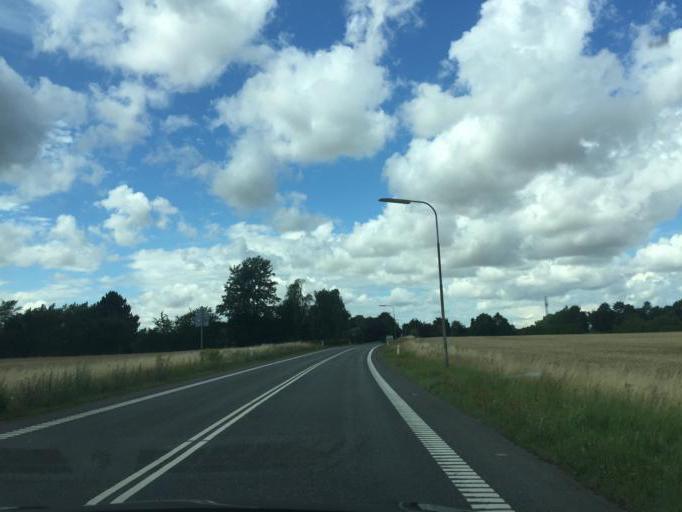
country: DK
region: South Denmark
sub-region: Odense Kommune
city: Stige
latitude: 55.4512
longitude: 10.3734
